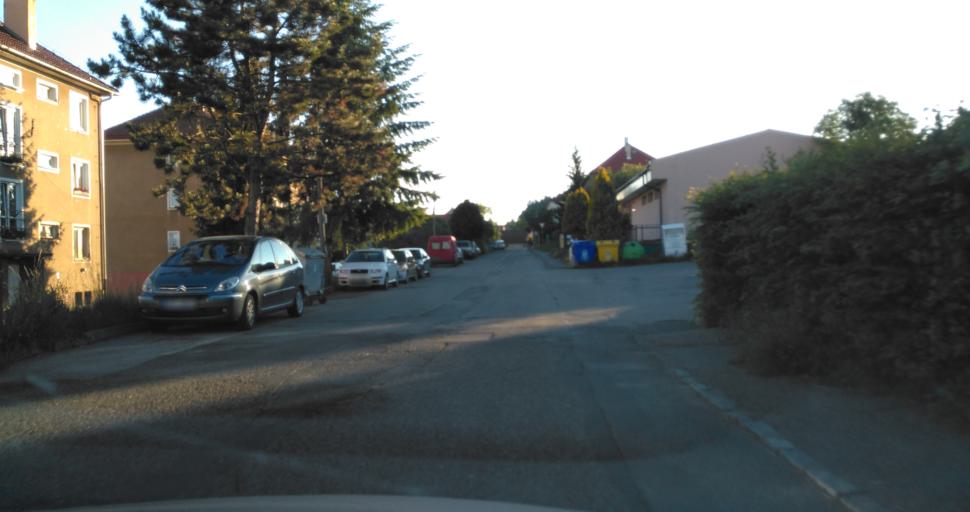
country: CZ
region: Central Bohemia
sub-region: Okres Beroun
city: Kraluv Dvur
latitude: 49.9073
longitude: 14.0365
